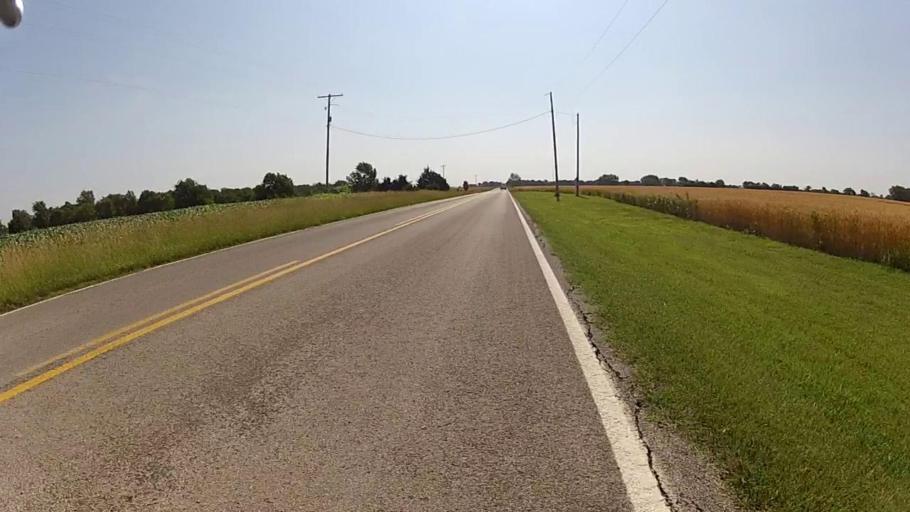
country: US
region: Kansas
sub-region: Montgomery County
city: Independence
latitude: 37.1930
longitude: -95.7549
